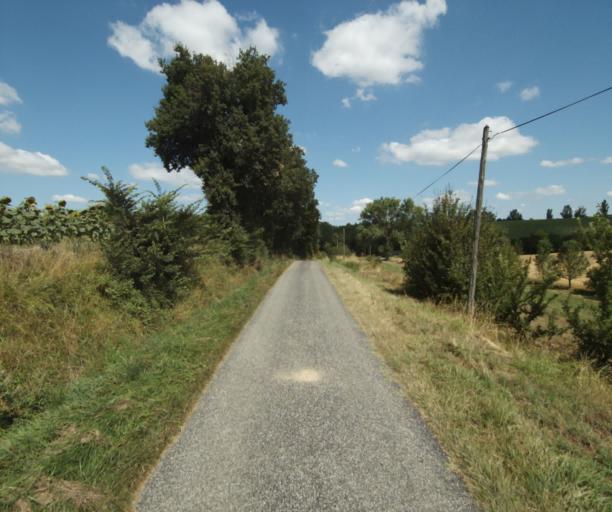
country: FR
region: Midi-Pyrenees
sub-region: Departement de la Haute-Garonne
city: Auriac-sur-Vendinelle
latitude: 43.4785
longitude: 1.7964
